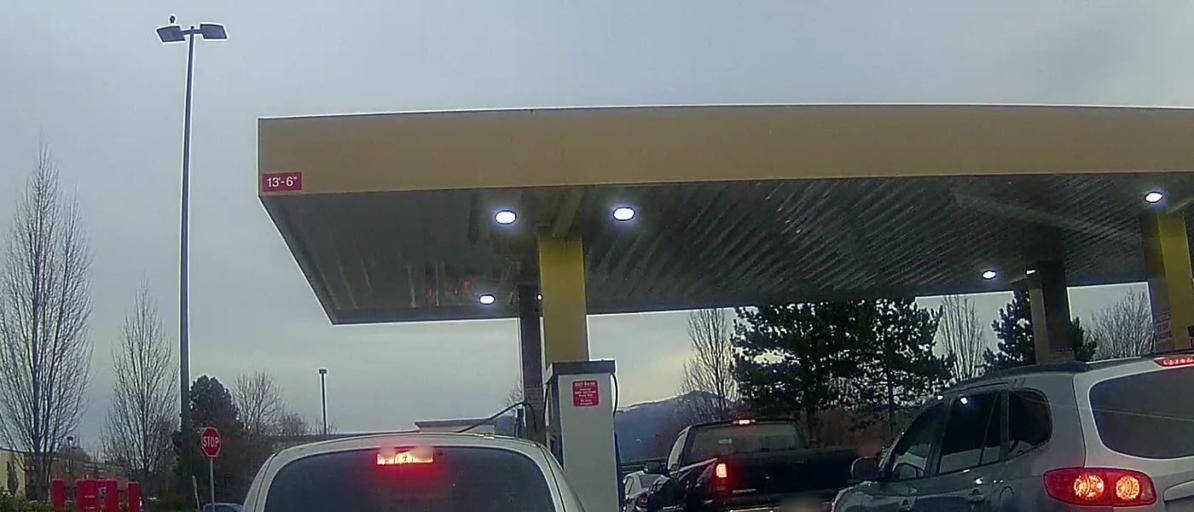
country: US
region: Washington
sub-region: Skagit County
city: Big Lake
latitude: 48.4317
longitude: -122.2721
